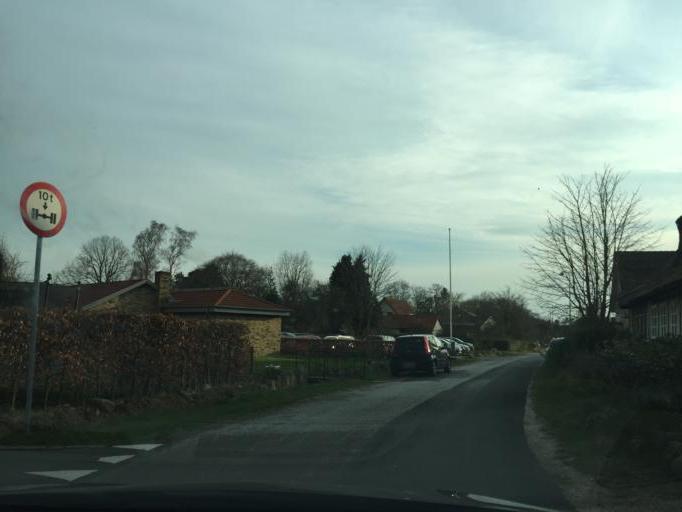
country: DK
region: South Denmark
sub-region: Kerteminde Kommune
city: Langeskov
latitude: 55.3413
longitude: 10.5470
